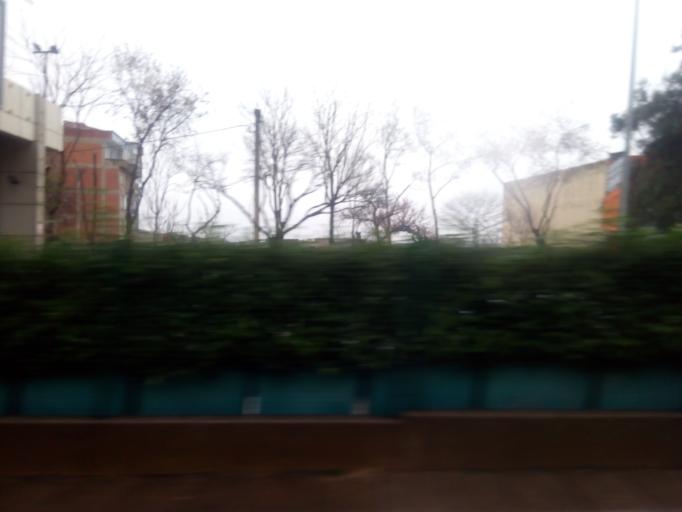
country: TR
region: Bursa
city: Yildirim
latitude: 40.2017
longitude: 29.0360
